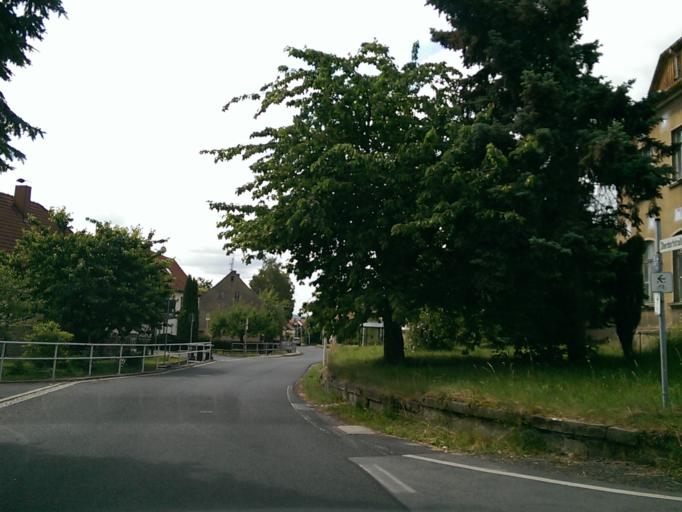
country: DE
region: Saxony
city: Mittelherwigsdorf
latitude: 50.9338
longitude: 14.7687
